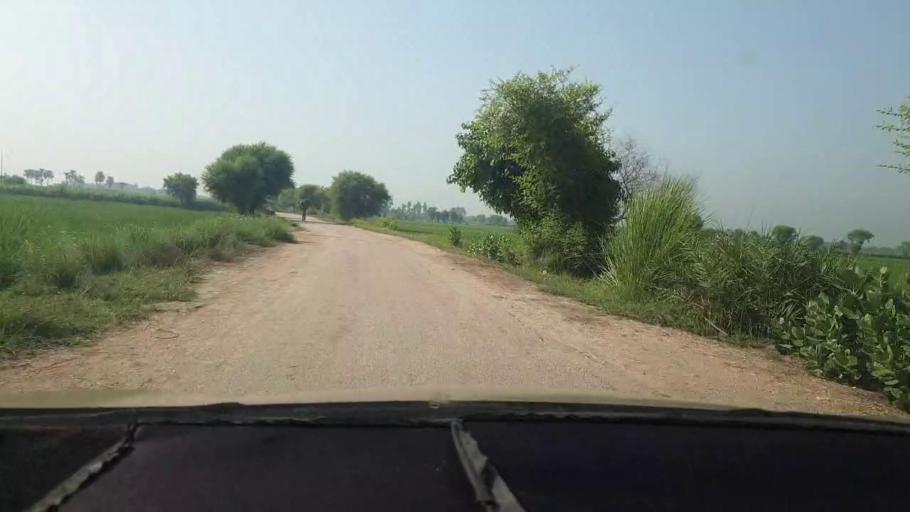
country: PK
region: Sindh
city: Kambar
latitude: 27.6177
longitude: 68.0904
